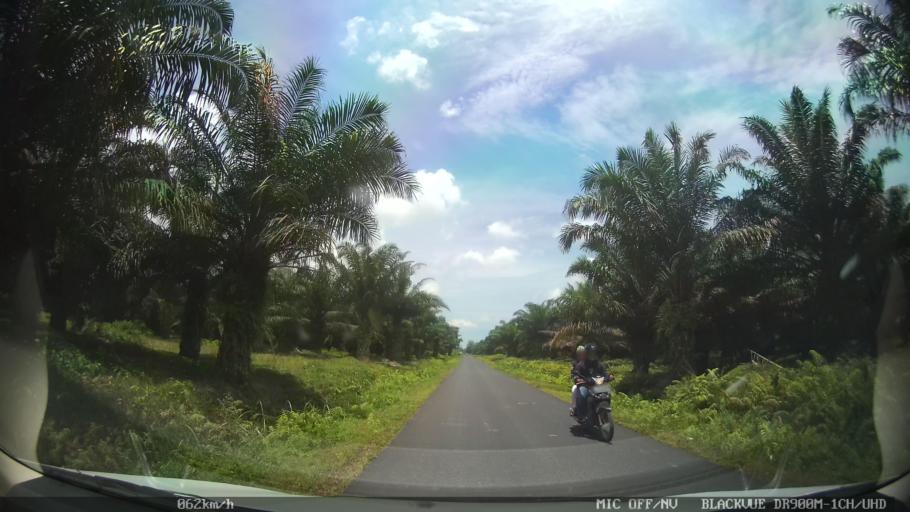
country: ID
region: North Sumatra
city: Percut
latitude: 3.5379
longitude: 98.8652
